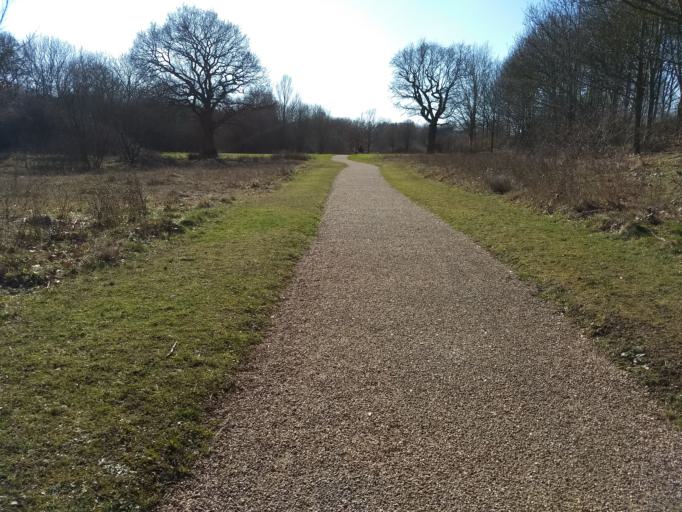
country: GB
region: England
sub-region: Milton Keynes
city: Shenley Church End
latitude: 52.0040
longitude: -0.7893
